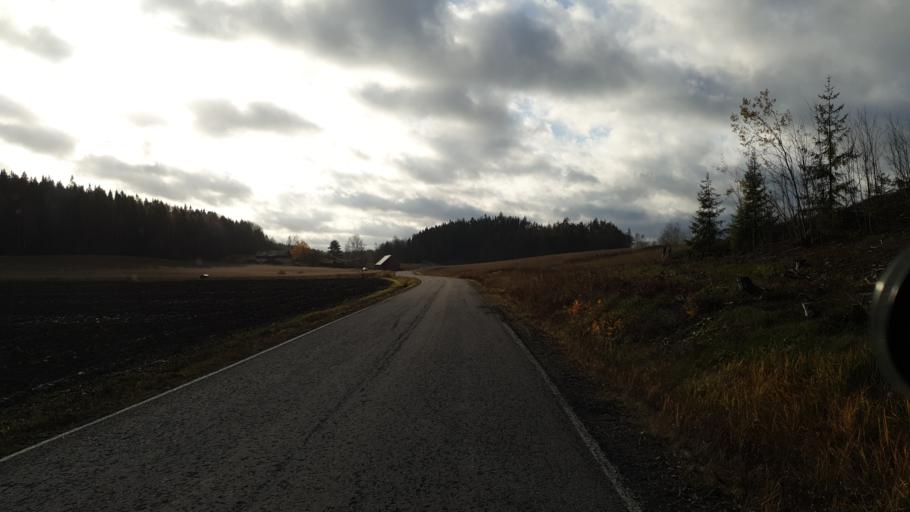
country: FI
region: Uusimaa
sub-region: Helsinki
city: Siuntio
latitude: 60.2573
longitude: 24.2987
